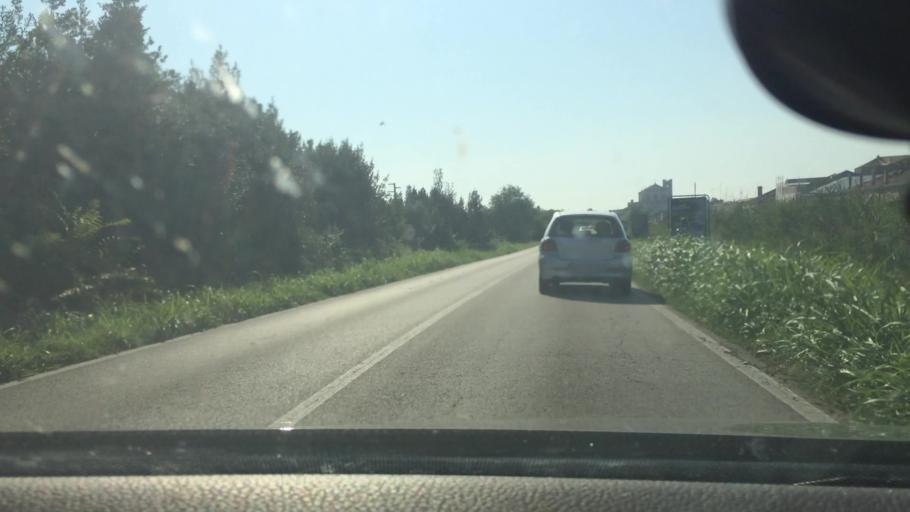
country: IT
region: Emilia-Romagna
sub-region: Provincia di Ferrara
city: Comacchio
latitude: 44.7002
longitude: 12.1735
